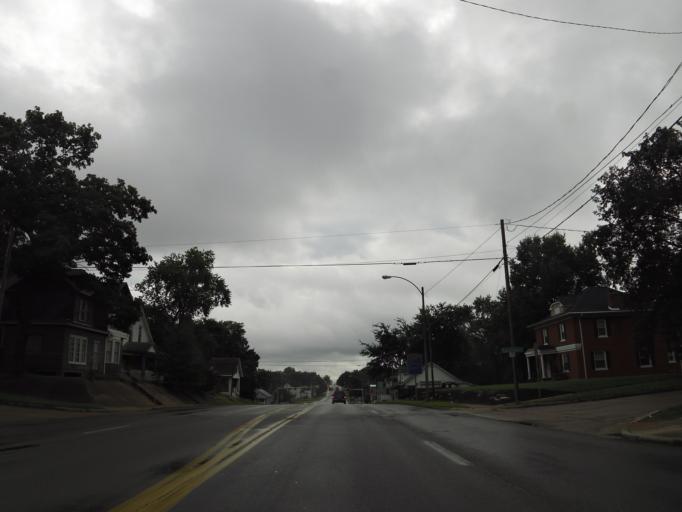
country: US
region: Missouri
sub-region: Cape Girardeau County
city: Cape Girardeau
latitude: 37.3021
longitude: -89.5383
